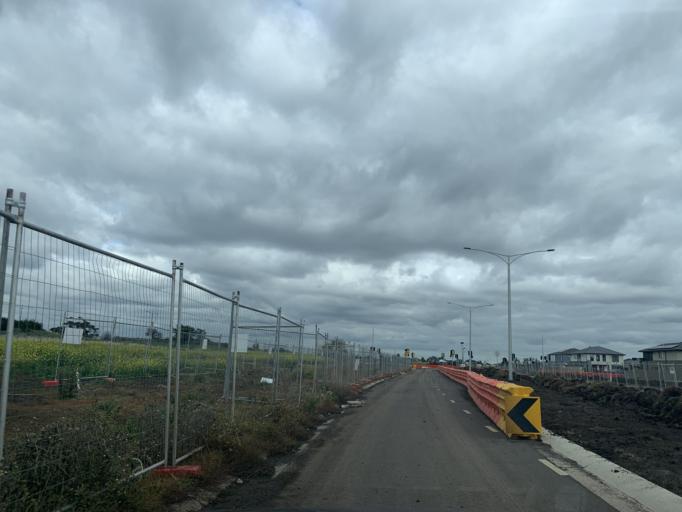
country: AU
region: Victoria
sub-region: Hume
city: Craigieburn
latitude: -37.5993
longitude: 145.0005
